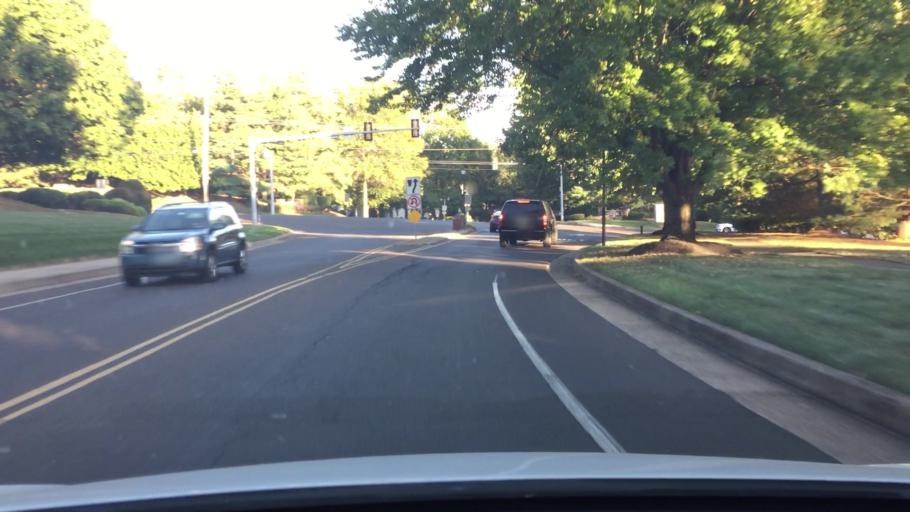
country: US
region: Pennsylvania
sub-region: Bucks County
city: Newtown
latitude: 40.2167
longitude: -74.9459
